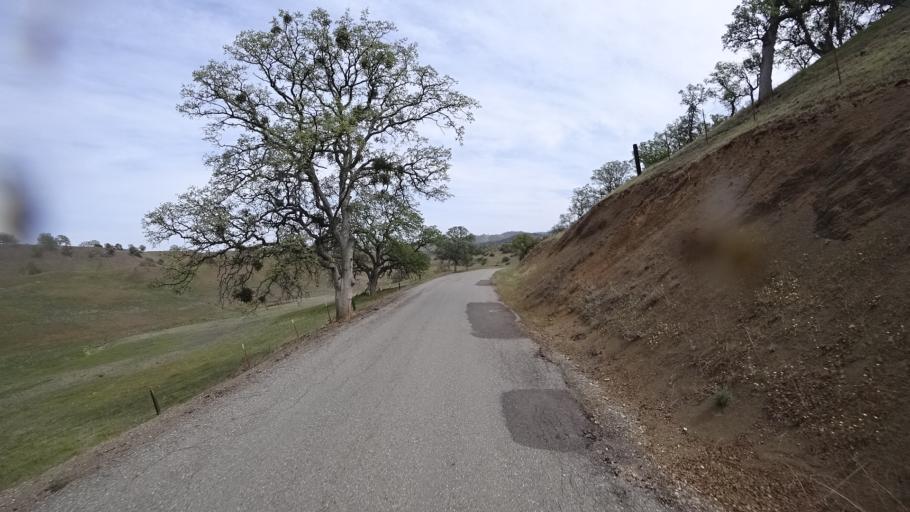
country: US
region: California
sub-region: Glenn County
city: Willows
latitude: 39.6103
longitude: -122.5630
